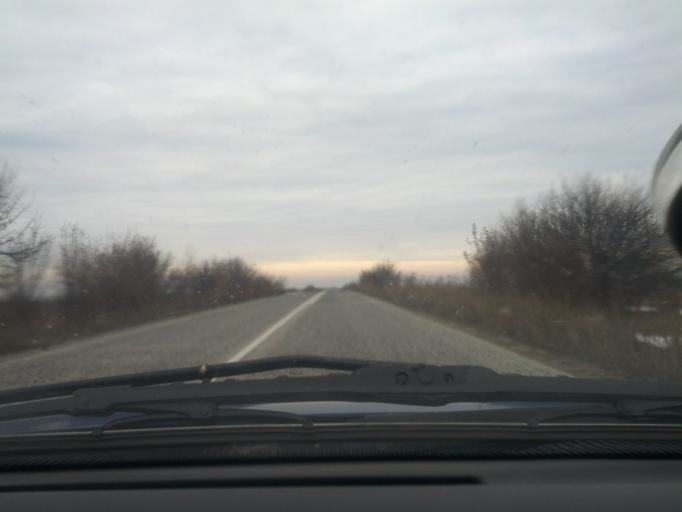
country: BG
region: Vratsa
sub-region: Obshtina Borovan
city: Borovan
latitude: 43.4019
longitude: 23.7295
